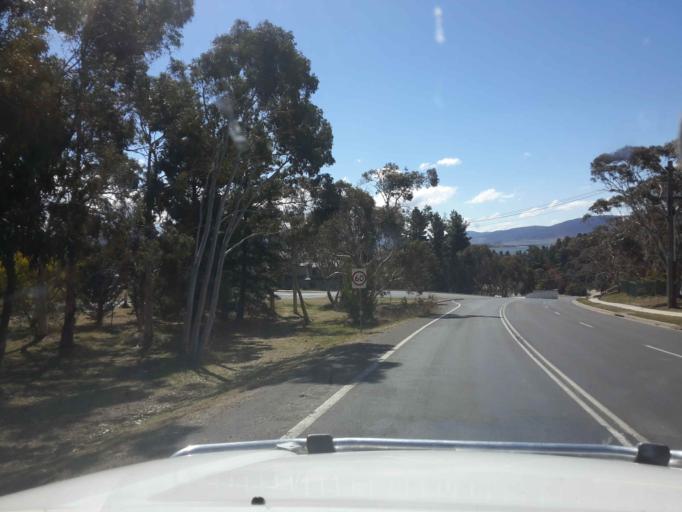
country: AU
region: New South Wales
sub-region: Snowy River
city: Jindabyne
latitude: -36.4186
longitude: 148.6105
